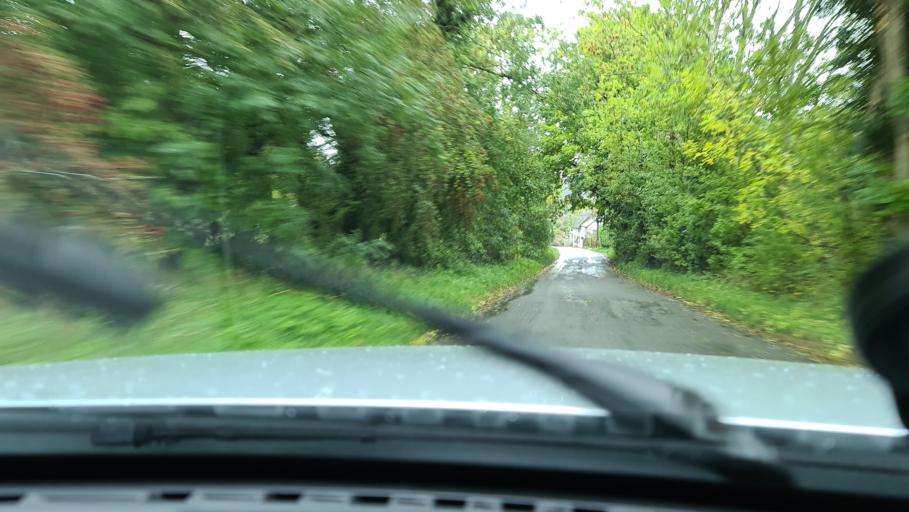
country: GB
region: England
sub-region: Oxfordshire
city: Deddington
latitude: 51.9253
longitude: -1.3680
